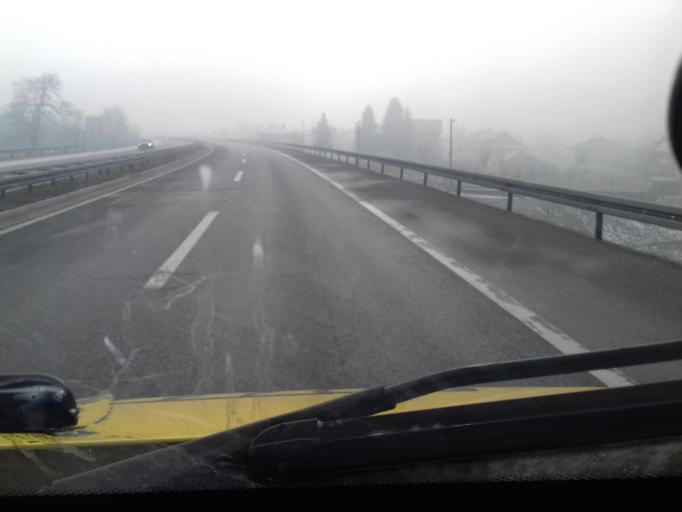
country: BA
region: Federation of Bosnia and Herzegovina
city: Ilijas
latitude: 43.9485
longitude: 18.2551
